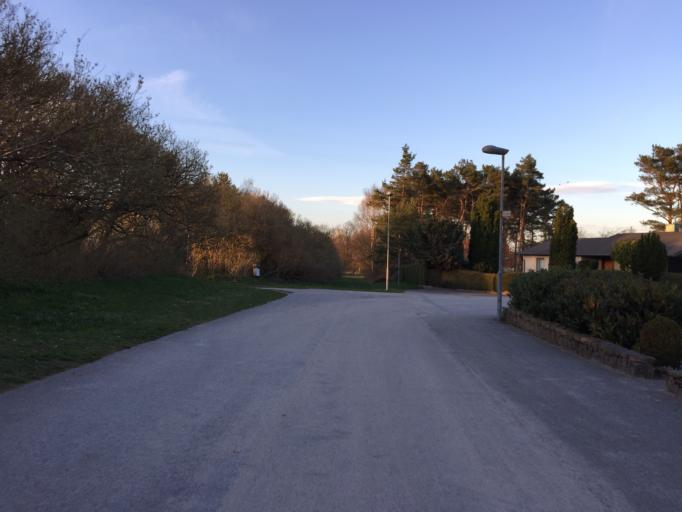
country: SE
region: Skane
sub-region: Lunds Kommun
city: Veberod
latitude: 55.6397
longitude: 13.4907
